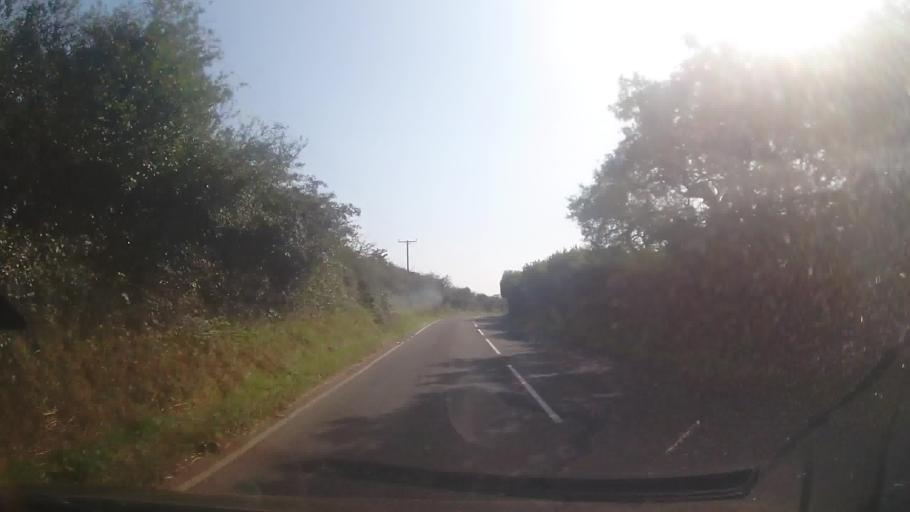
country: GB
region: Wales
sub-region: Pembrokeshire
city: Scleddau
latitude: 51.9772
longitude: -5.0078
